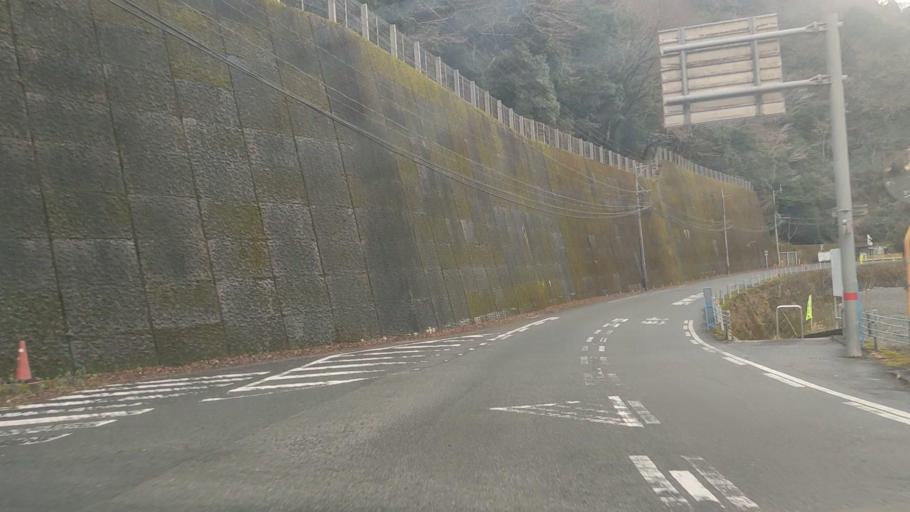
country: JP
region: Kumamoto
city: Hitoyoshi
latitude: 32.4184
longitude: 130.8525
